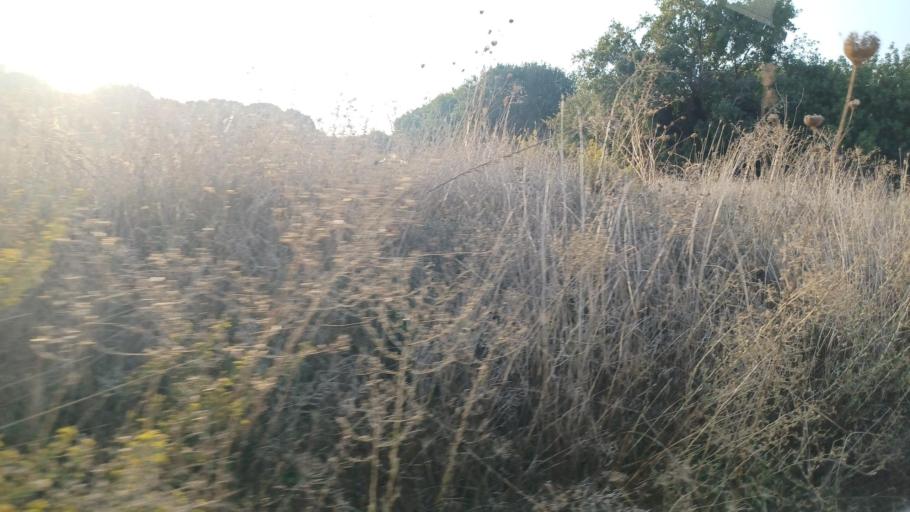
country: CY
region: Pafos
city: Polis
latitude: 34.9672
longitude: 32.4858
